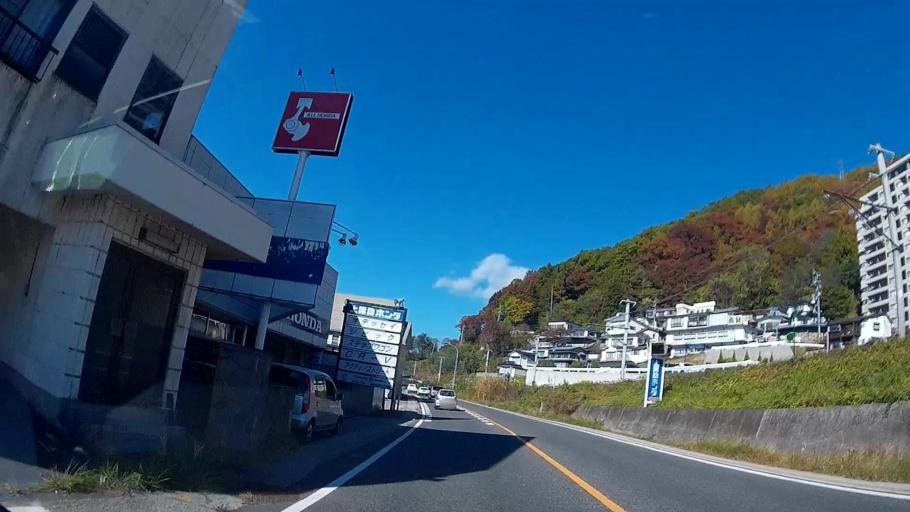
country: JP
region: Nagano
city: Suwa
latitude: 36.0667
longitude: 138.1029
